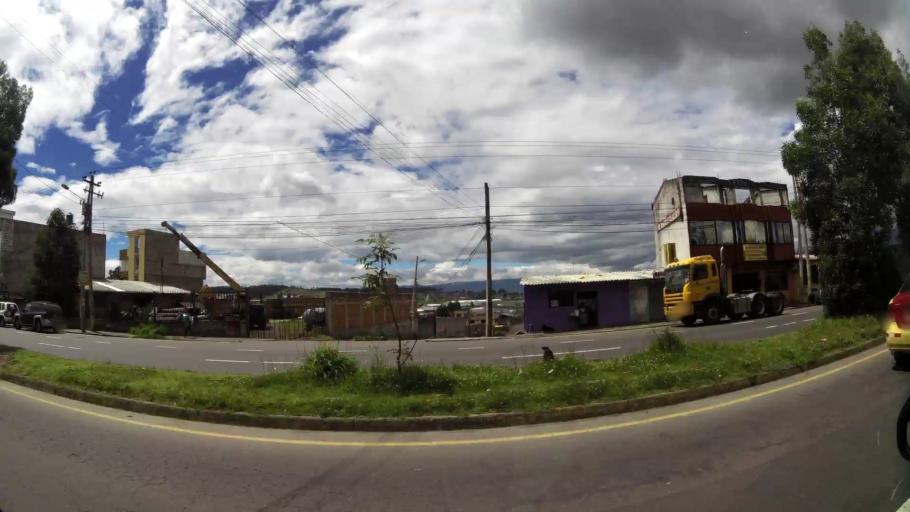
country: EC
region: Pichincha
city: Sangolqui
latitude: -0.3531
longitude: -78.5495
